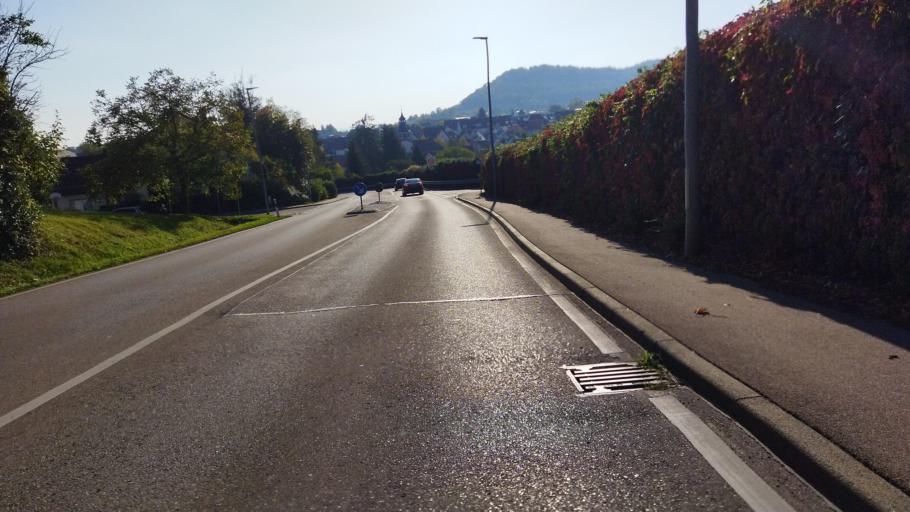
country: DE
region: Baden-Wuerttemberg
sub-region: Regierungsbezirk Stuttgart
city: Freudental
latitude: 49.0122
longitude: 9.0633
